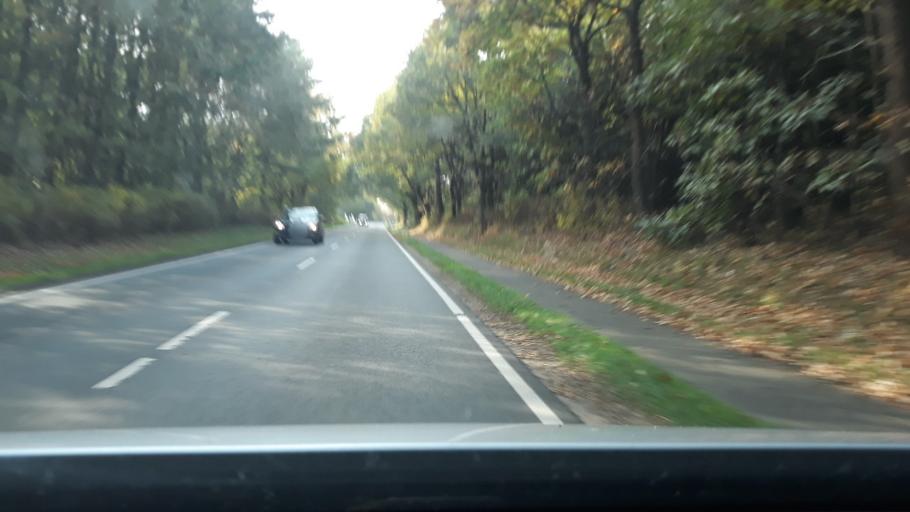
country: DE
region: Schleswig-Holstein
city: Owschlag
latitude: 54.3974
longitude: 9.5647
